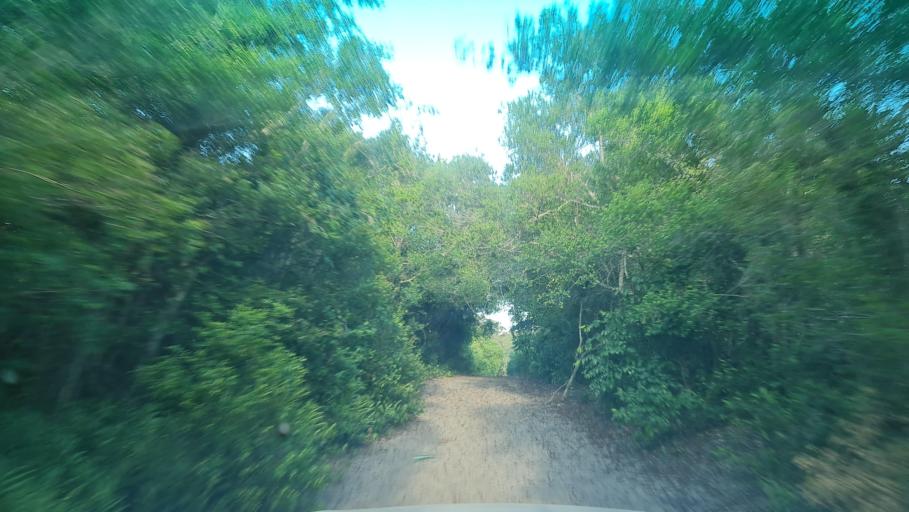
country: MZ
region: Gaza
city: Macia
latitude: -25.2285
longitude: 33.0170
